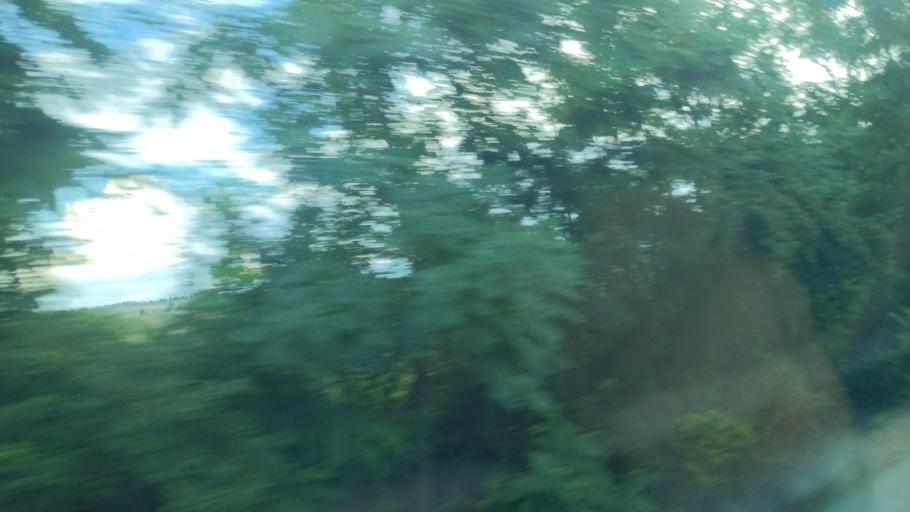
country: CZ
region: Central Bohemia
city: Uvaly
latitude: 50.0774
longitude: 14.7812
